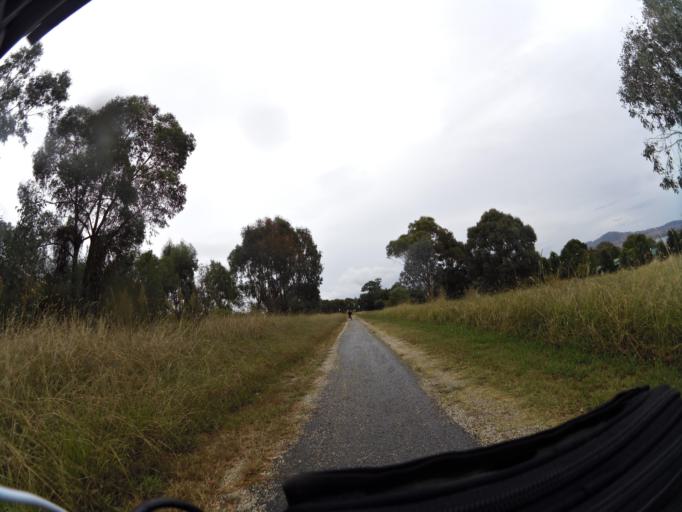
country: AU
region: New South Wales
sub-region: Albury Municipality
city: East Albury
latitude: -36.2252
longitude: 147.1062
